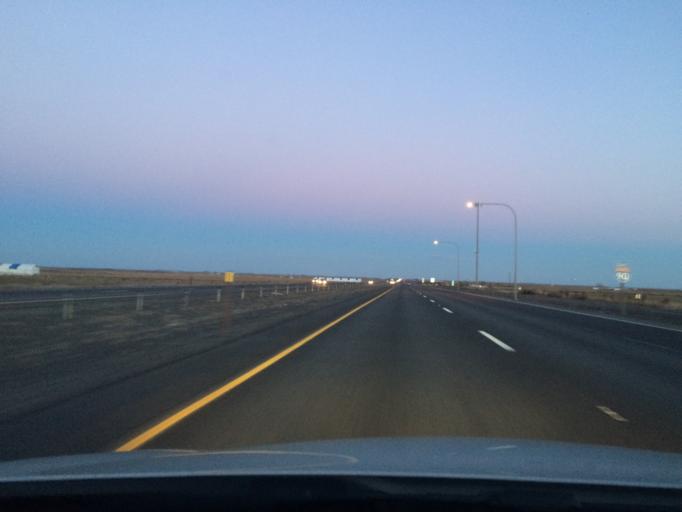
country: US
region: Washington
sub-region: Grant County
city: Quincy
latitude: 47.1035
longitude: -119.7627
